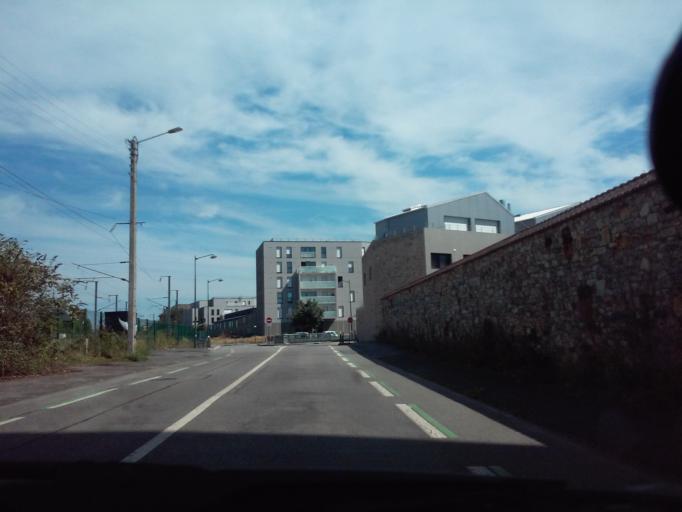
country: FR
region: Brittany
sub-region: Departement d'Ille-et-Vilaine
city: Rennes
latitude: 48.1019
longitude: -1.6957
